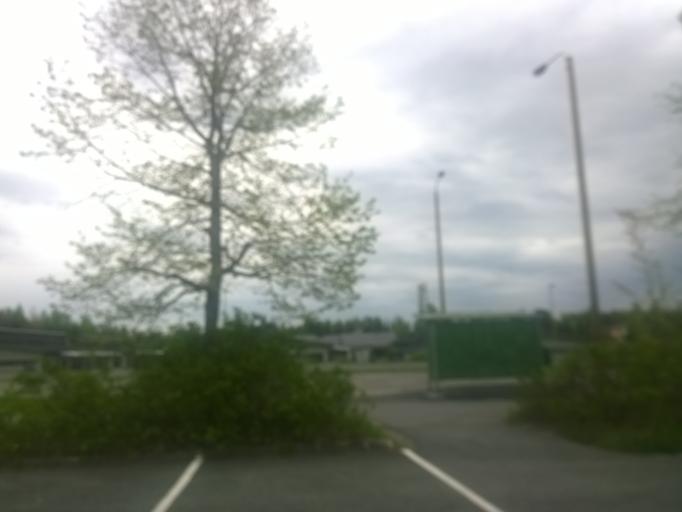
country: FI
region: Pirkanmaa
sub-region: Tampere
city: Lempaeaelae
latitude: 61.3316
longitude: 23.7488
